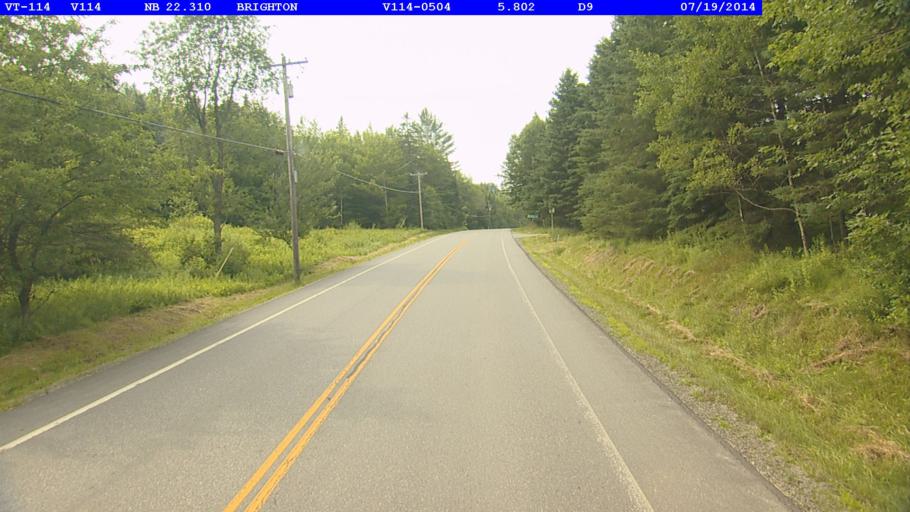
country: US
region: Vermont
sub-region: Caledonia County
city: Lyndonville
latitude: 44.8262
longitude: -71.9024
